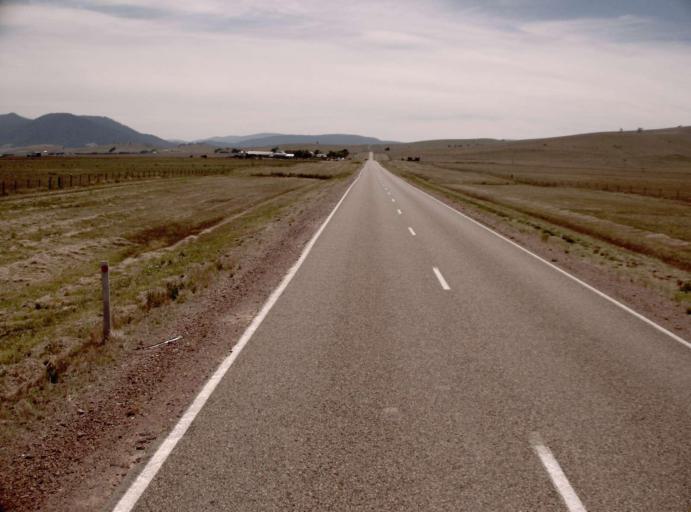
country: AU
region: Victoria
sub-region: Alpine
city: Mount Beauty
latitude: -37.0000
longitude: 147.6732
